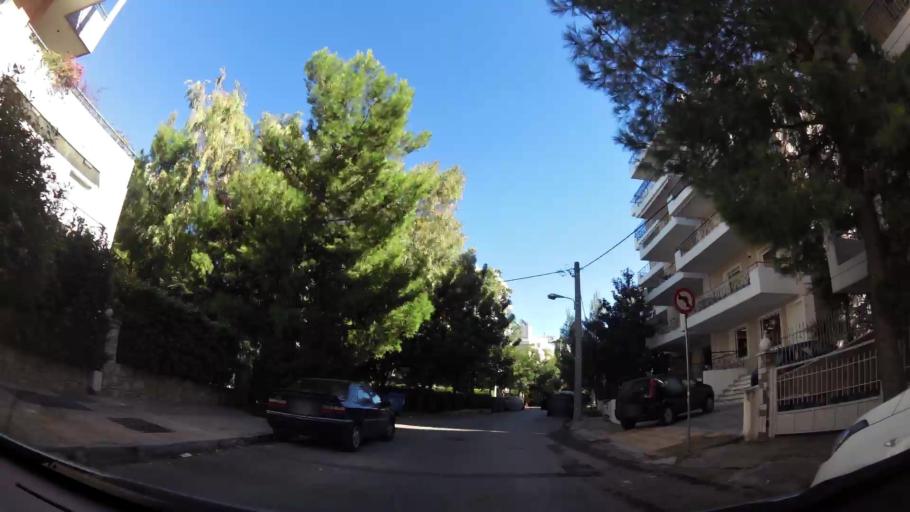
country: GR
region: Attica
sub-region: Nomarchia Athinas
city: Nea Erythraia
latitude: 38.0931
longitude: 23.8127
